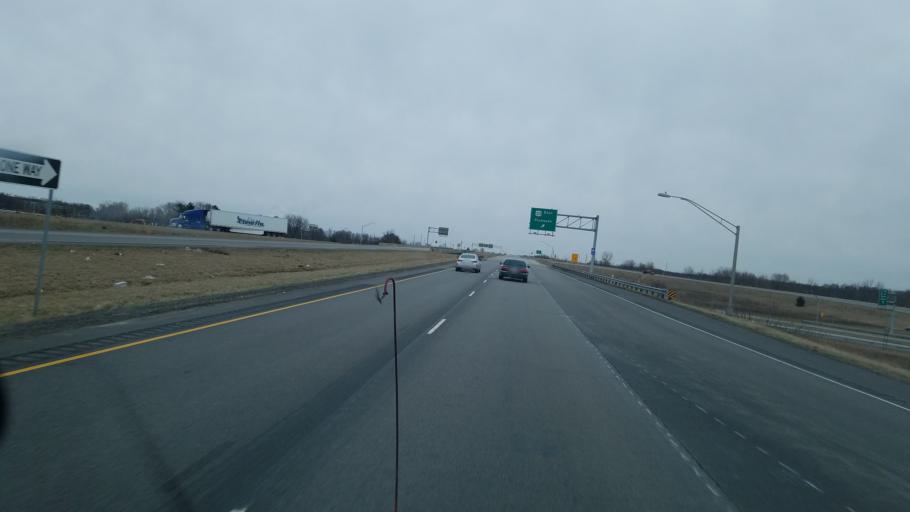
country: US
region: Indiana
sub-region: Porter County
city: Valparaiso
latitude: 41.4558
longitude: -87.0270
